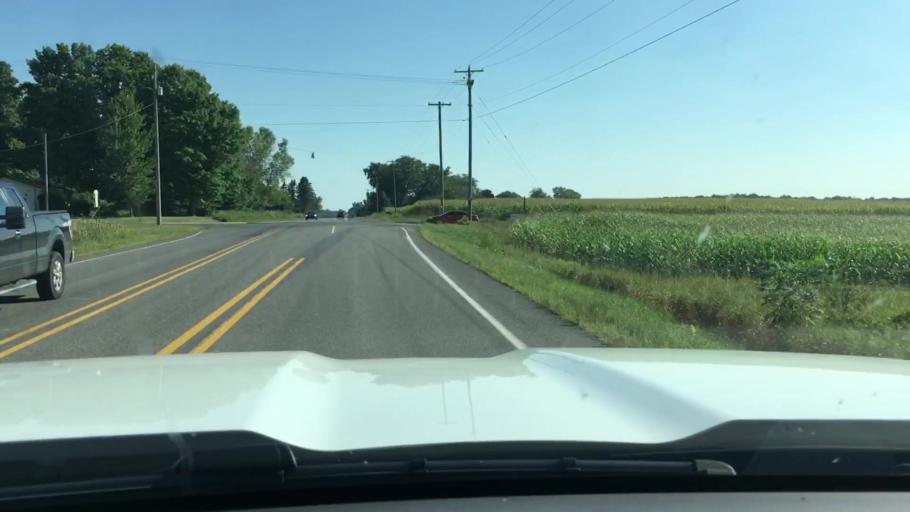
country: US
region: Michigan
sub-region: Muskegon County
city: Ravenna
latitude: 43.1629
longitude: -85.9279
